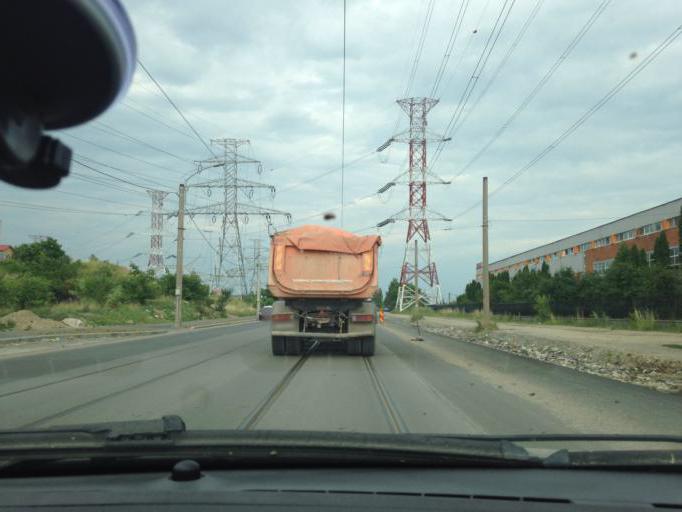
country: RO
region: Cluj
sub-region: Municipiul Cluj-Napoca
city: Cluj-Napoca
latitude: 46.7962
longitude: 23.6425
